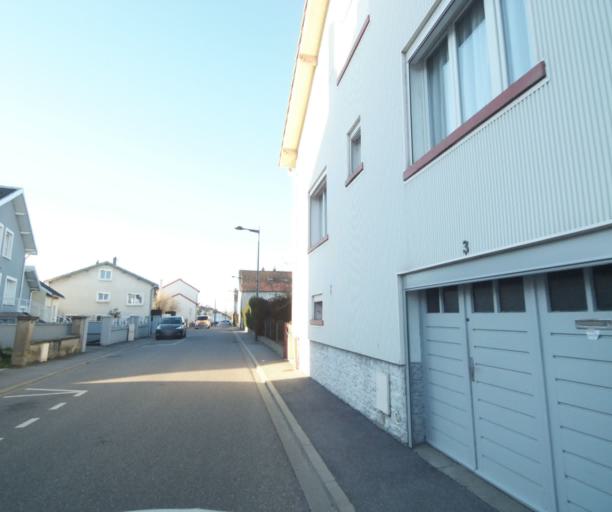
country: FR
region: Lorraine
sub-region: Departement de Meurthe-et-Moselle
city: Laneuveville-devant-Nancy
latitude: 48.6524
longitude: 6.2269
